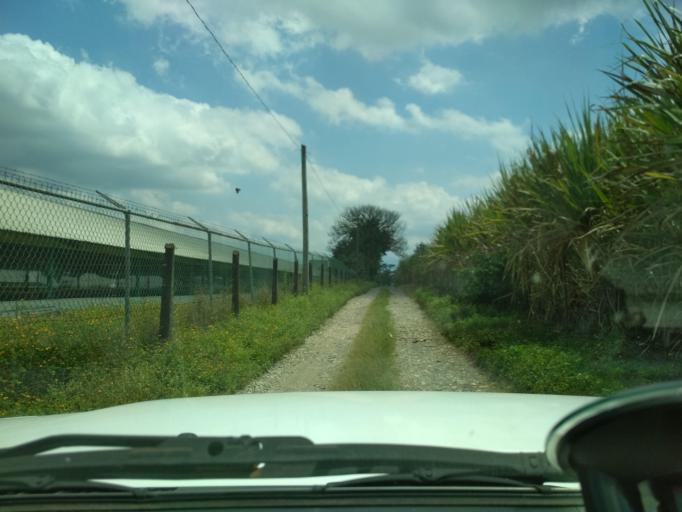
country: MX
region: Veracruz
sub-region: Fortin
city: Monte Salas
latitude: 18.9329
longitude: -97.0172
